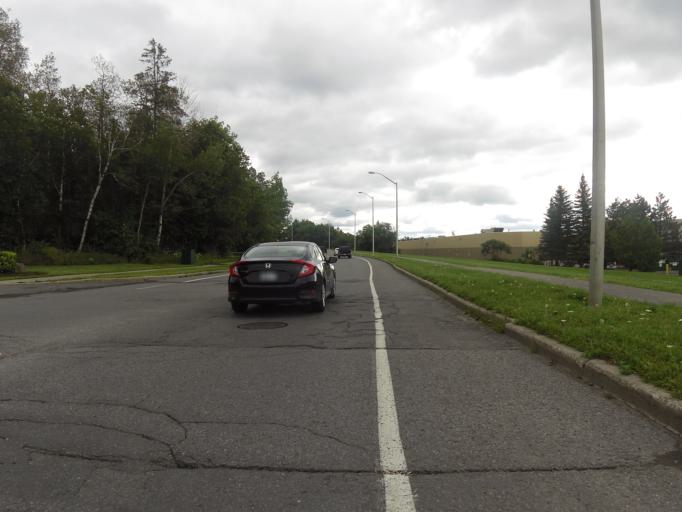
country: CA
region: Ontario
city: Bells Corners
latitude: 45.3124
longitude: -75.9146
